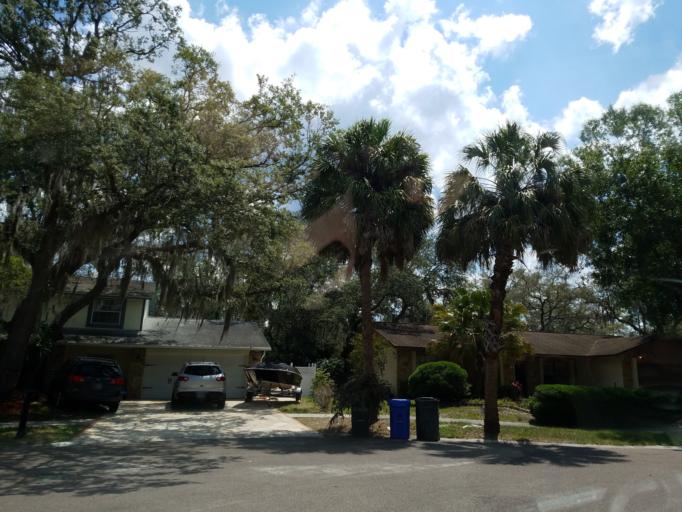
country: US
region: Florida
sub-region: Hillsborough County
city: Bloomingdale
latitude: 27.8835
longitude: -82.2701
